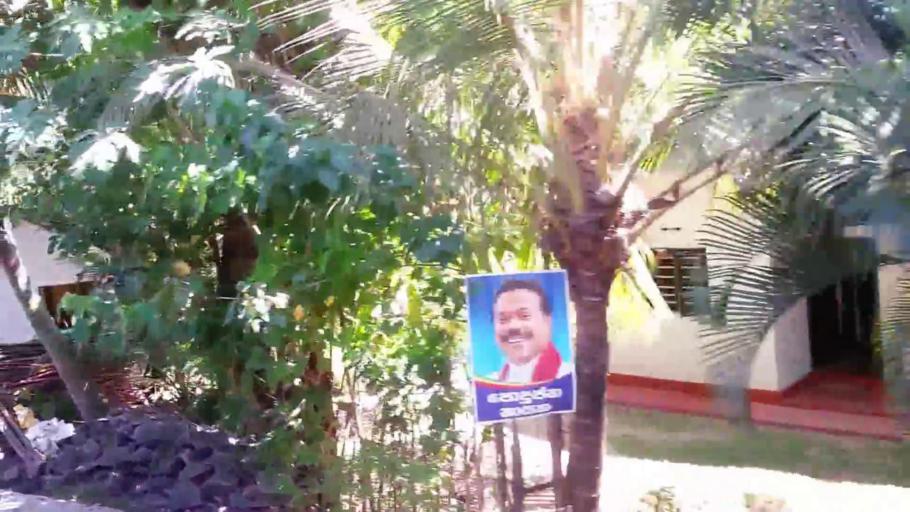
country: LK
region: Southern
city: Hikkaduwa
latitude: 6.1779
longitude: 80.0796
